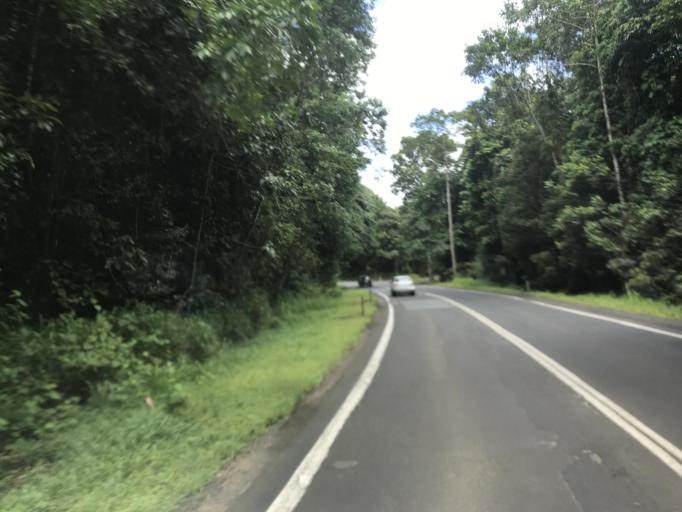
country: AU
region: Queensland
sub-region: Tablelands
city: Ravenshoe
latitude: -17.6005
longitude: 145.7587
